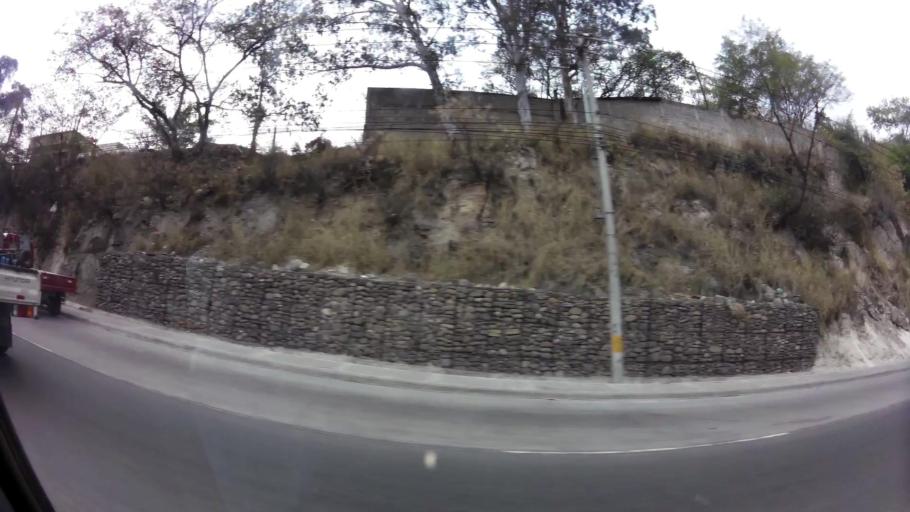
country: HN
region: Francisco Morazan
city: Tegucigalpa
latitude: 14.0828
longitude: -87.2179
